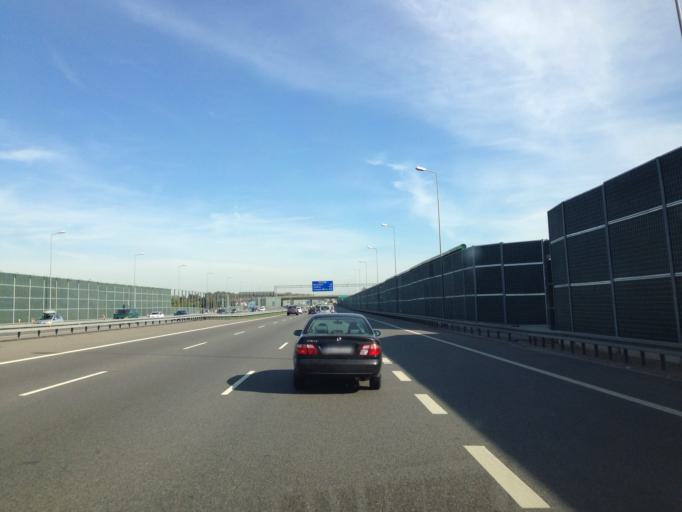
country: PL
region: Masovian Voivodeship
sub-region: Powiat warszawski zachodni
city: Ozarow Mazowiecki
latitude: 52.1905
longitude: 20.7902
